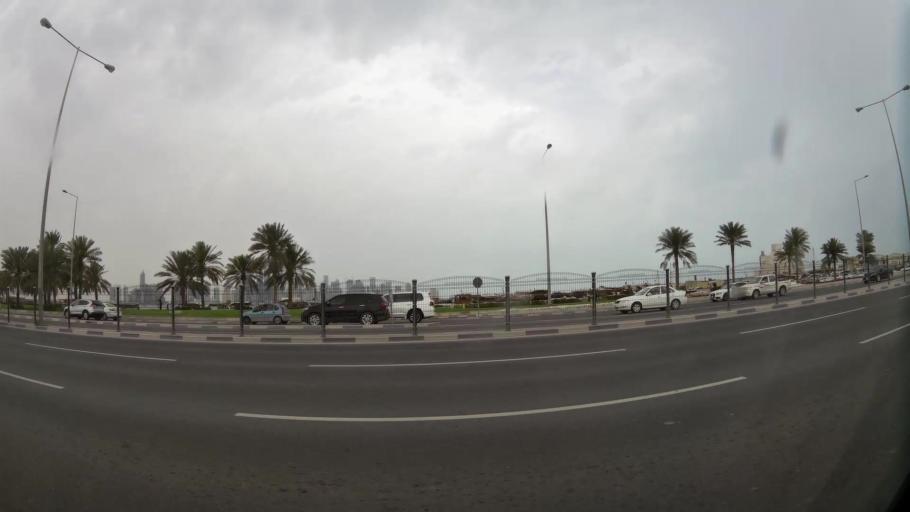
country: QA
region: Baladiyat ad Dawhah
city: Doha
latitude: 25.2913
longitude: 51.5323
